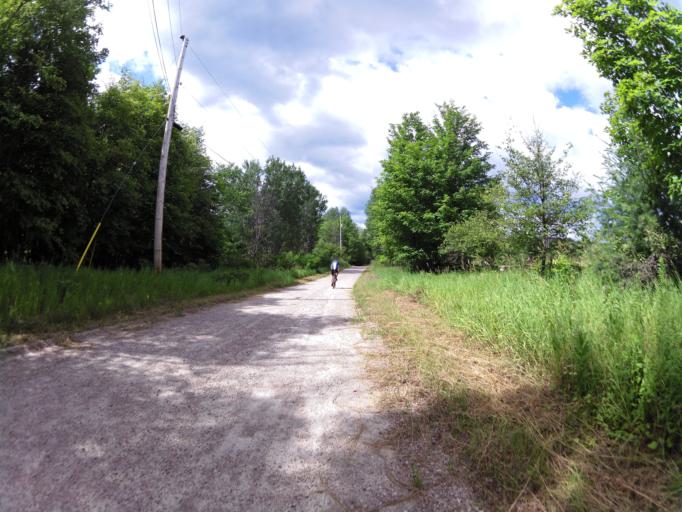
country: CA
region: Ontario
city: Perth
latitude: 45.0594
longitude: -76.4837
